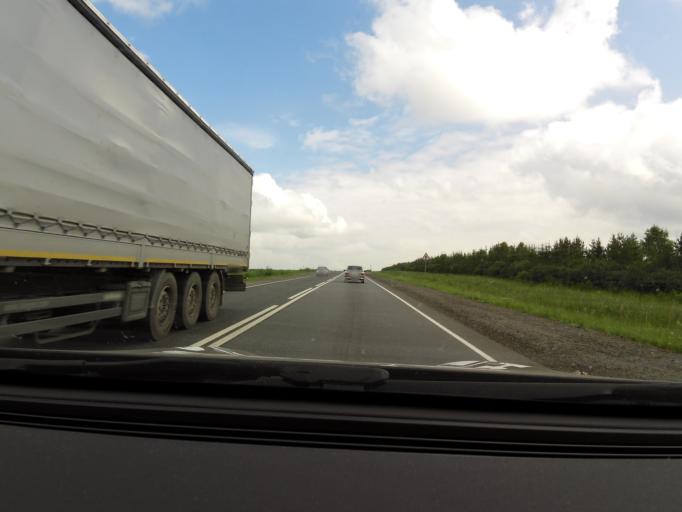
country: RU
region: Perm
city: Suksun
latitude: 57.1606
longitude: 57.2288
